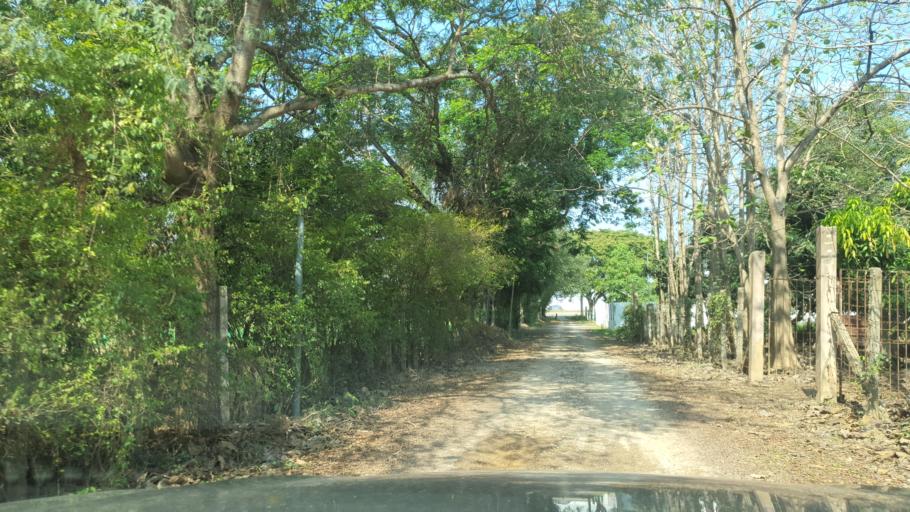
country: TH
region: Chiang Mai
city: Saraphi
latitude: 18.7310
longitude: 99.0407
